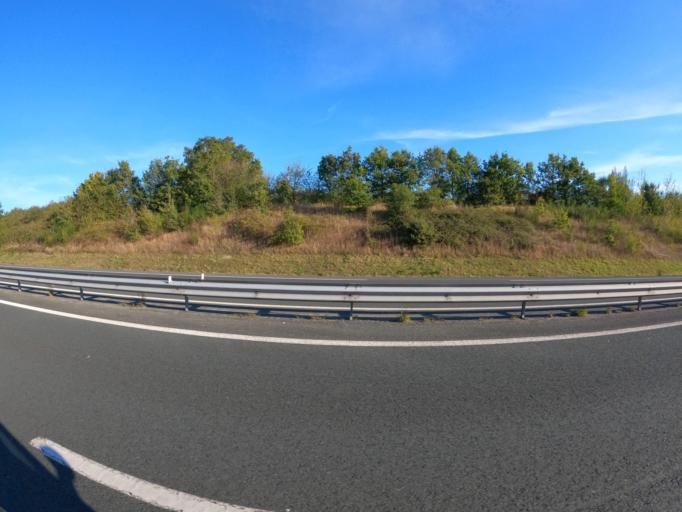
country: FR
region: Pays de la Loire
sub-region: Departement de Maine-et-Loire
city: La Tessoualle
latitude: 47.0366
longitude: -0.8498
